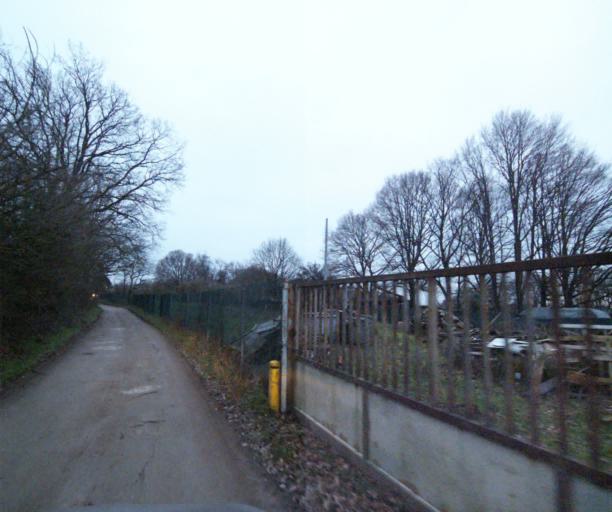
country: FR
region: Ile-de-France
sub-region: Departement de Seine-et-Marne
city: Longperrier
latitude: 49.0611
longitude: 2.6612
